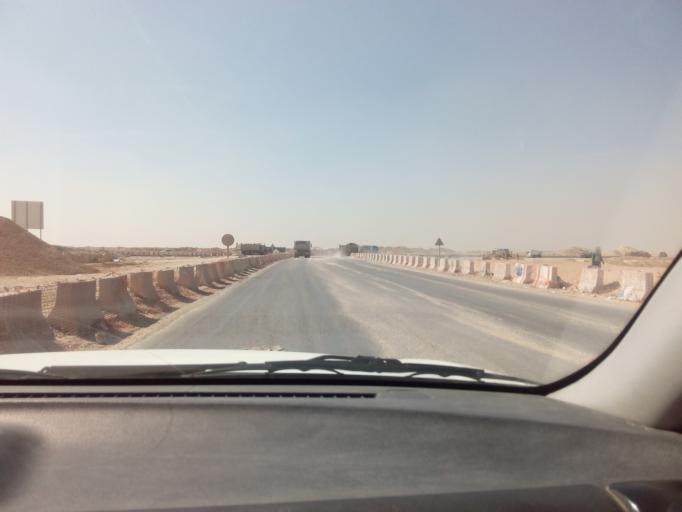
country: SA
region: Ar Riyad
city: Riyadh
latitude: 24.6358
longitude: 46.8745
